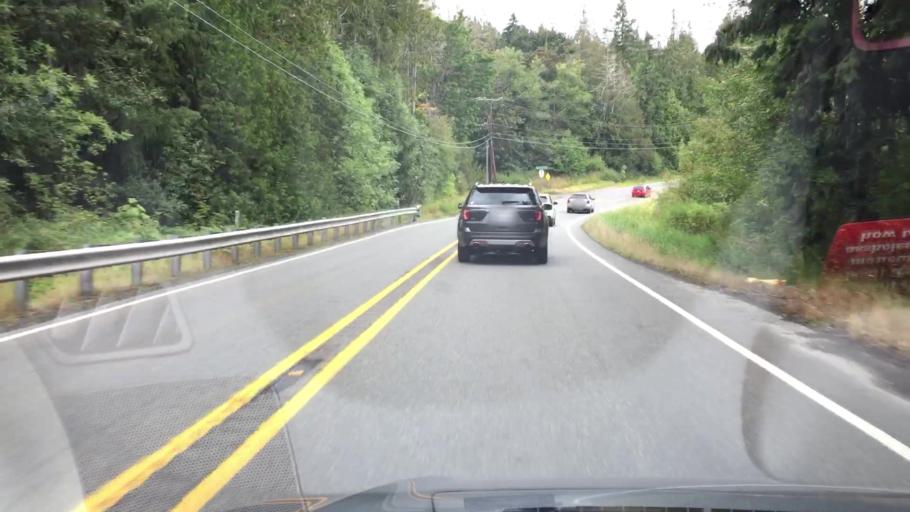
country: US
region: Washington
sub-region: Pierce County
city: Eatonville
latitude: 46.9411
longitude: -122.2812
